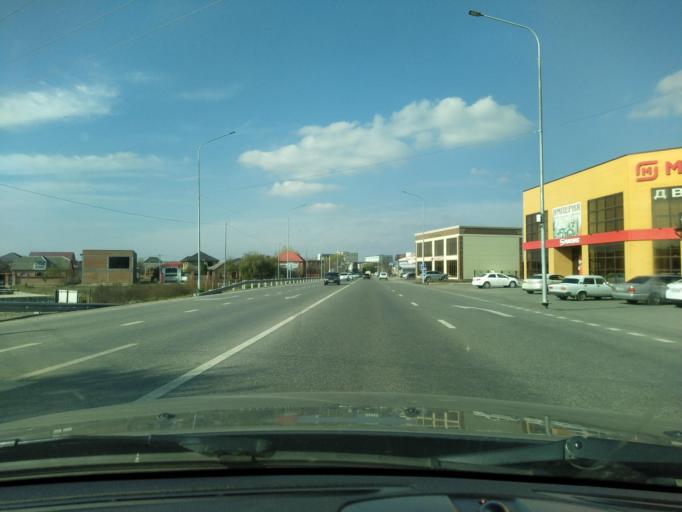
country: RU
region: Ingushetiya
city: Magas
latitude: 43.1959
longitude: 44.7601
